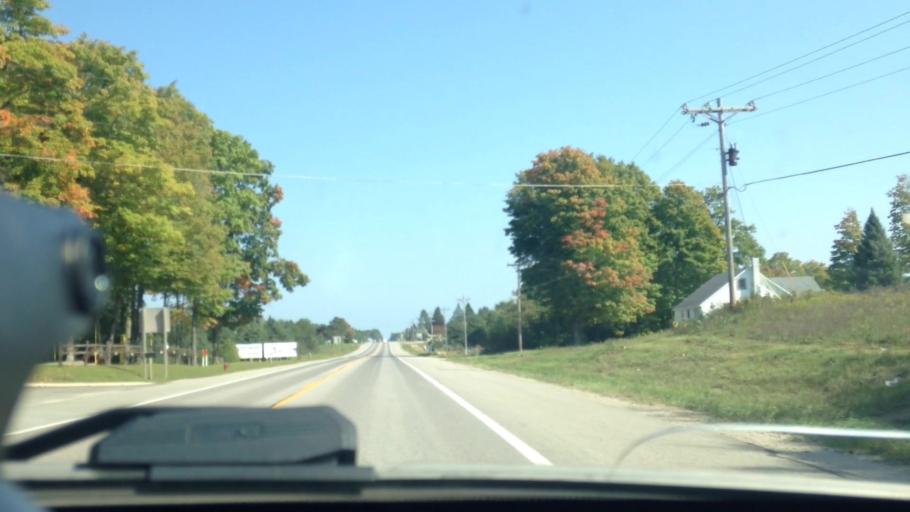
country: US
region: Michigan
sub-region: Luce County
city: Newberry
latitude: 46.3034
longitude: -85.5044
